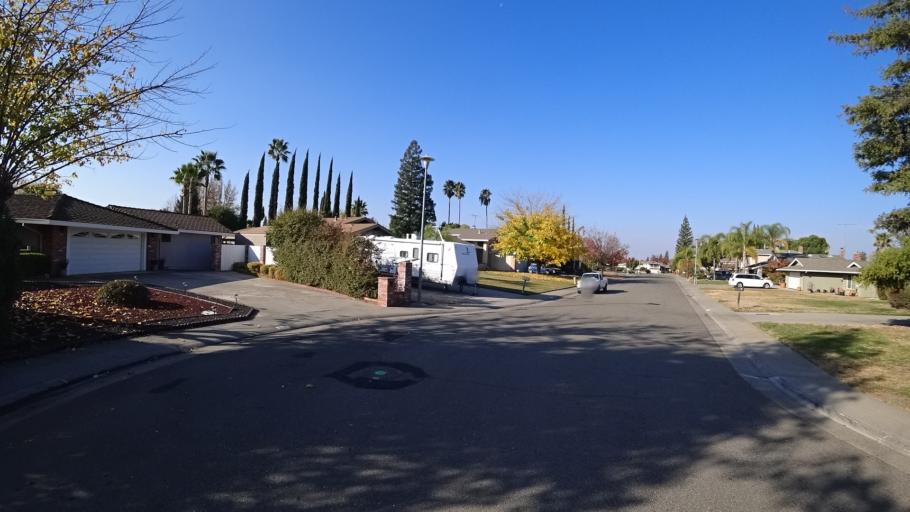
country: US
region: California
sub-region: Sacramento County
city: Citrus Heights
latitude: 38.7159
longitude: -121.2598
